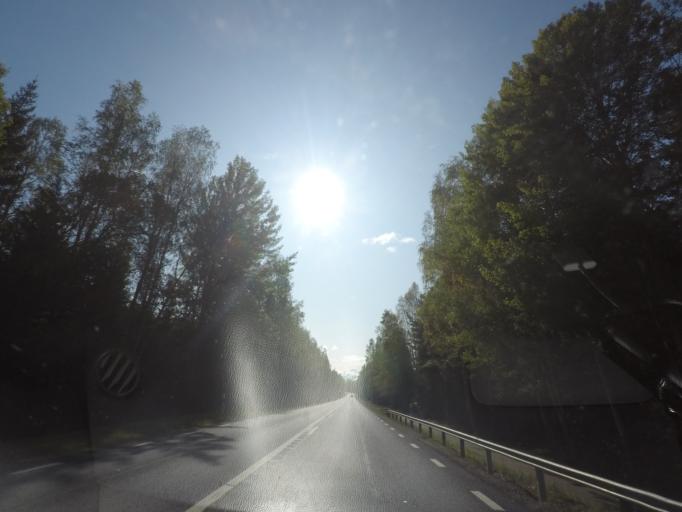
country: SE
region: Vaestmanland
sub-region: Skinnskattebergs Kommun
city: Skinnskatteberg
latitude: 59.8193
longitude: 15.5322
